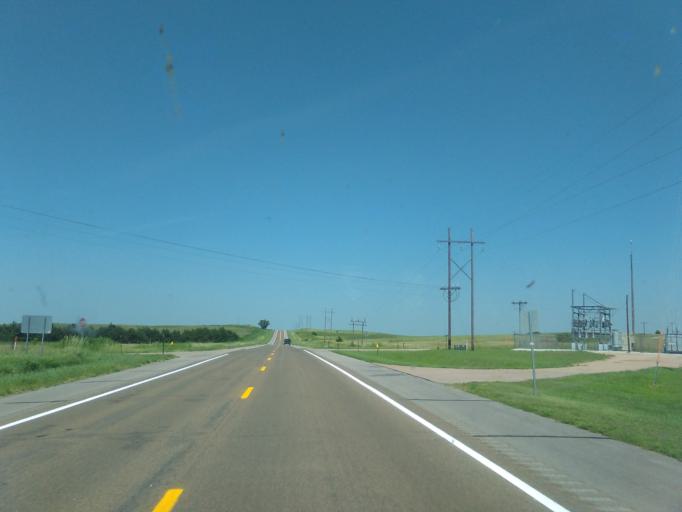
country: US
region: Nebraska
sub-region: Lincoln County
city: North Platte
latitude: 40.7603
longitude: -100.7296
